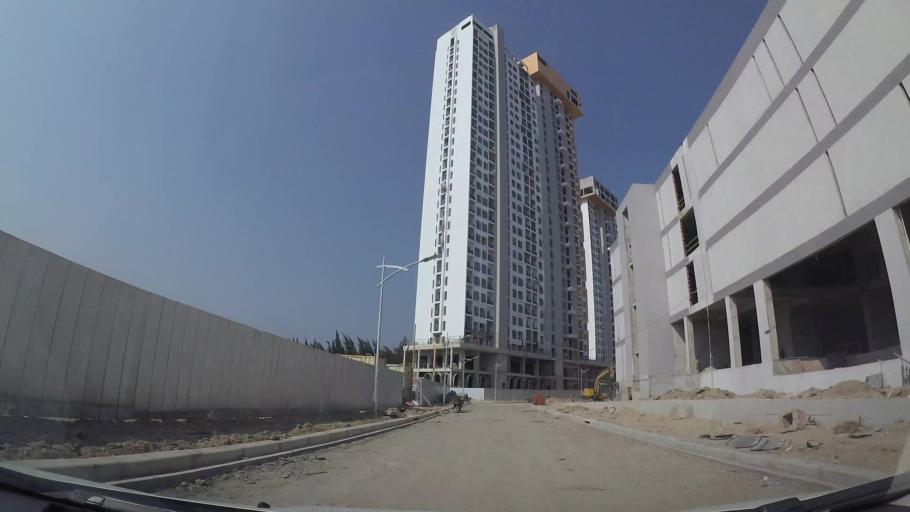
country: VN
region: Da Nang
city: Ngu Hanh Son
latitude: 15.9636
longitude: 108.2783
